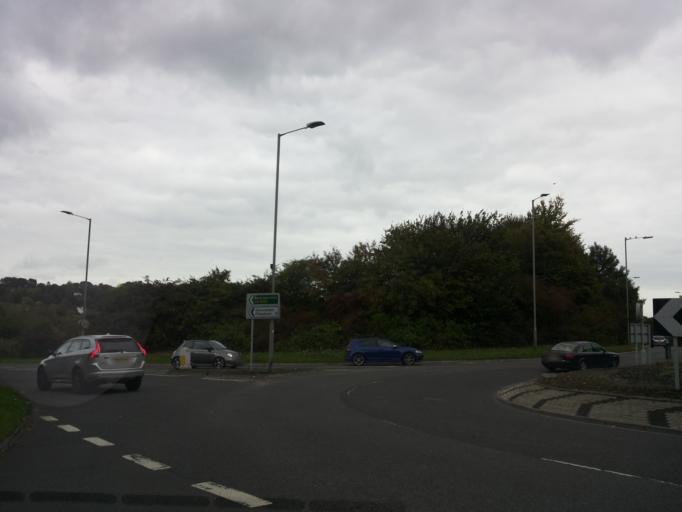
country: GB
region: England
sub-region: Buckinghamshire
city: Amersham
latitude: 51.6635
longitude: -0.6134
